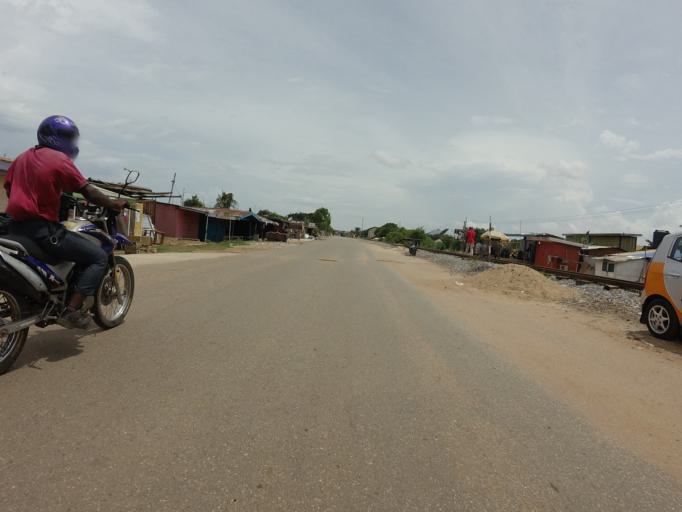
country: GH
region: Greater Accra
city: Accra
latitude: 5.6058
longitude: -0.2080
